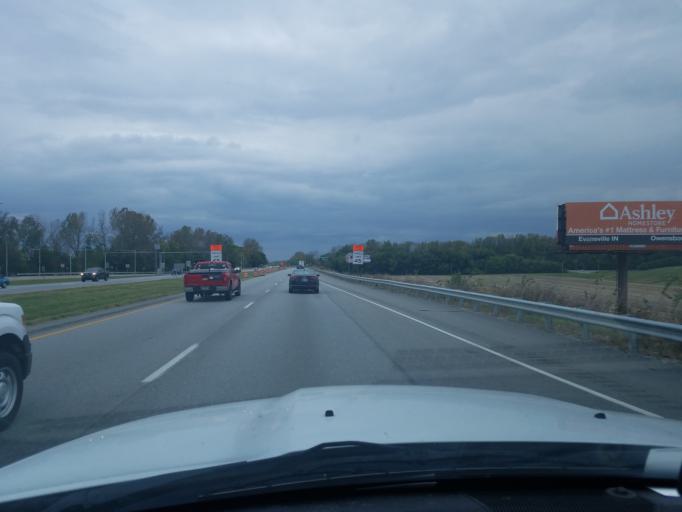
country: US
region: Indiana
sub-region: Vanderburgh County
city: Evansville
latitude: 37.9186
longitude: -87.5489
